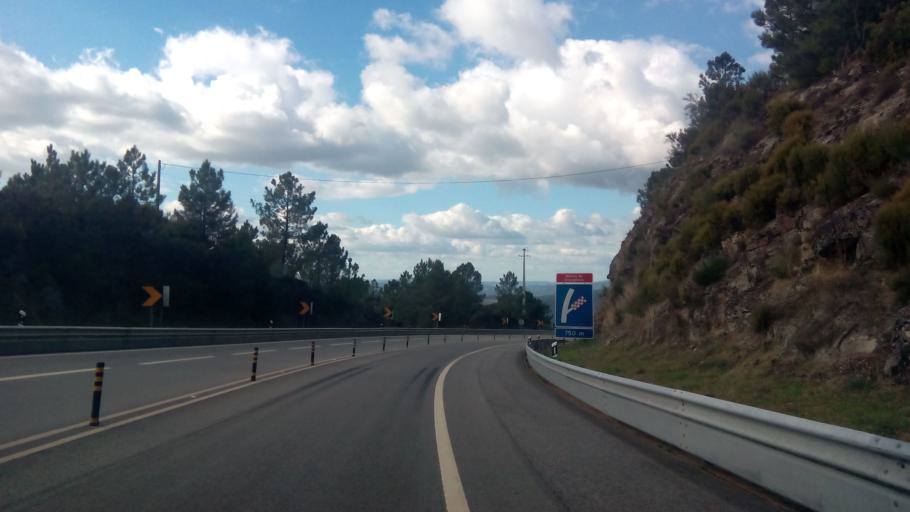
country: PT
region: Porto
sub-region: Baiao
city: Valadares
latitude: 41.2560
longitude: -7.9676
